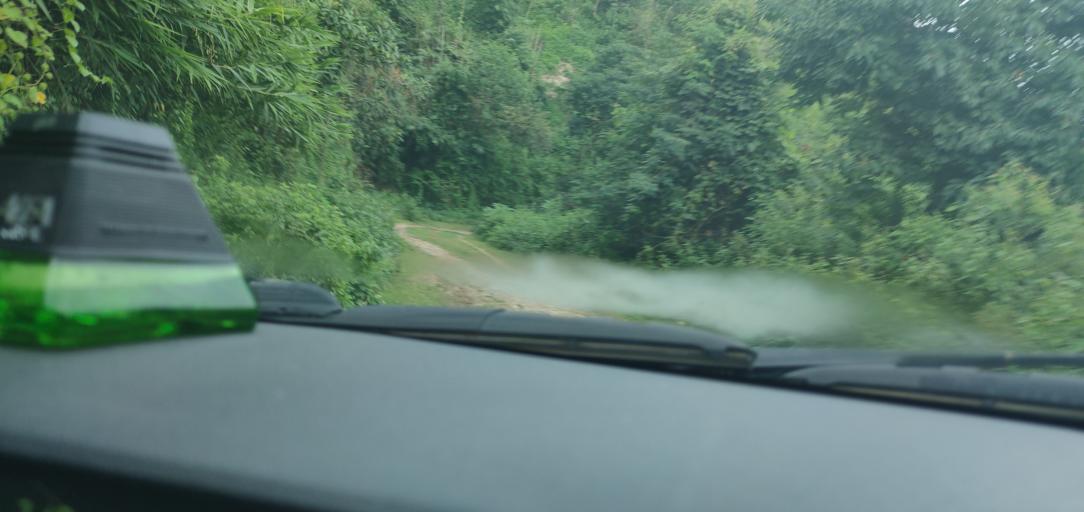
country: LA
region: Phongsali
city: Phongsali
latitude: 21.4415
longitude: 102.3273
